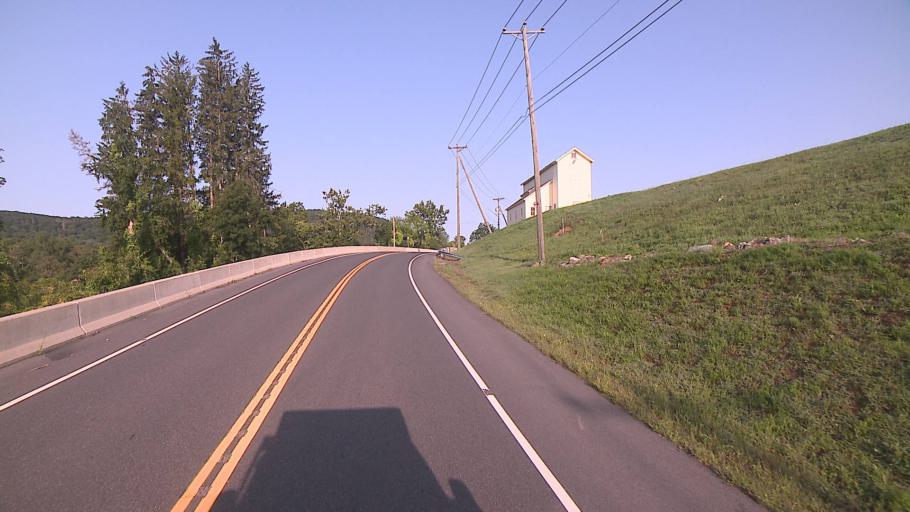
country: US
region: Connecticut
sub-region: Litchfield County
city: Kent
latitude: 41.6599
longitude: -73.4911
